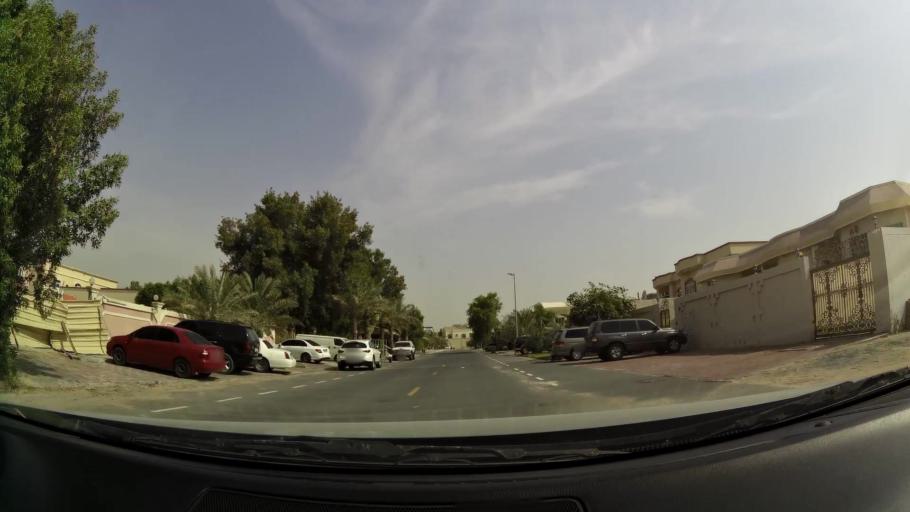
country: AE
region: Ash Shariqah
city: Sharjah
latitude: 25.2529
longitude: 55.4311
